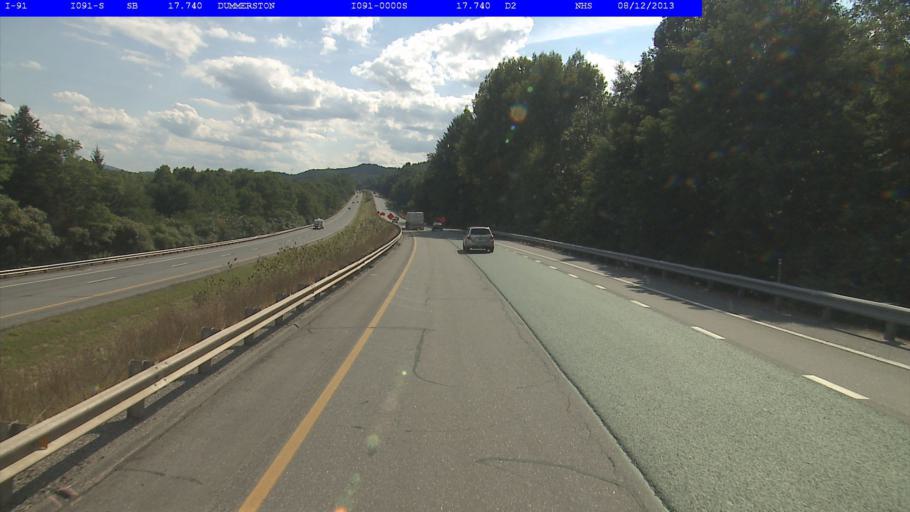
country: US
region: New Hampshire
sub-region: Cheshire County
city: Westmoreland
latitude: 42.9623
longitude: -72.5280
